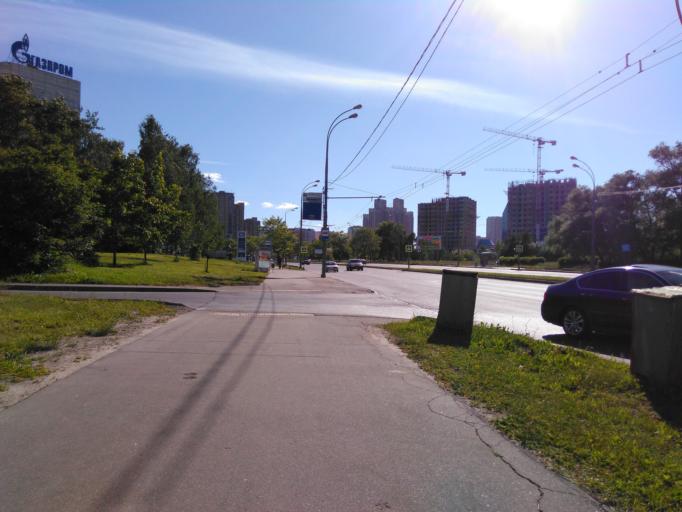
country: RU
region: Moscow
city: Troparevo
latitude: 55.6678
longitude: 37.4897
